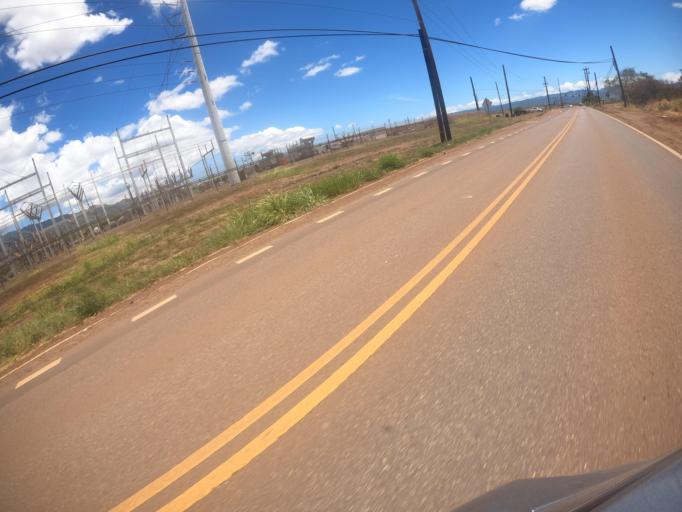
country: US
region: Hawaii
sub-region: Honolulu County
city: Royal Kunia
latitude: 21.3715
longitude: -158.0452
